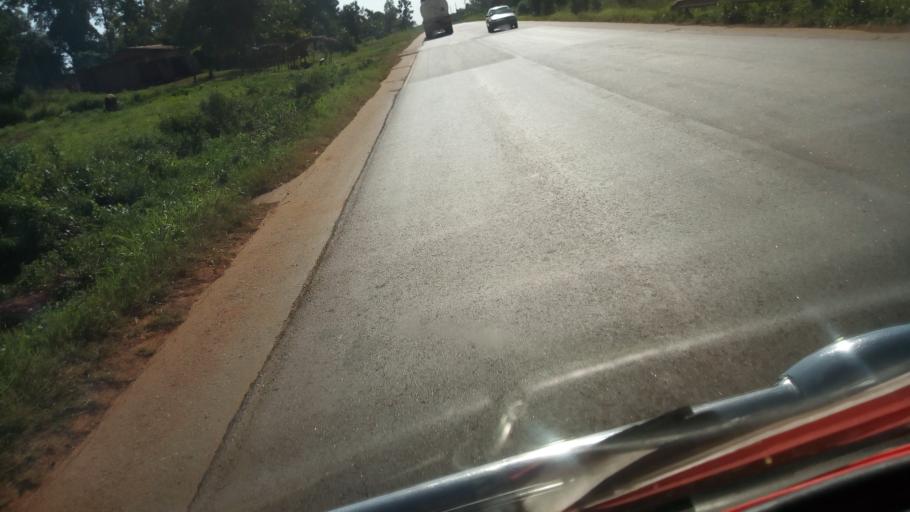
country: UG
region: Eastern Region
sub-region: Bugiri District
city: Bugiri
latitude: 0.5271
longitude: 33.8494
